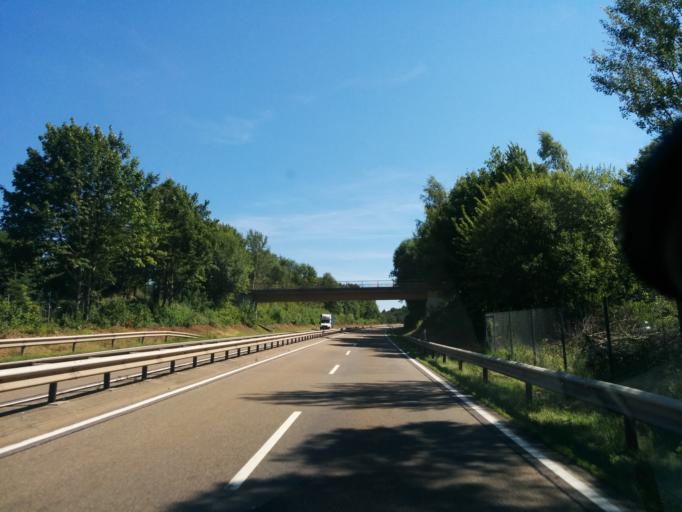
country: DE
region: Rheinland-Pfalz
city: Miellen
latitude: 50.3475
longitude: 7.6384
